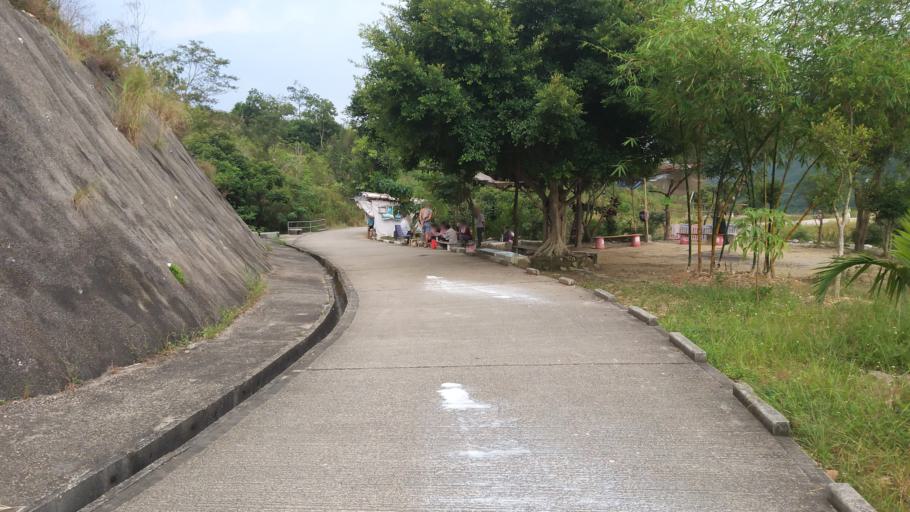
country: HK
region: Tuen Mun
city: Tuen Mun
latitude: 22.4078
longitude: 113.9530
